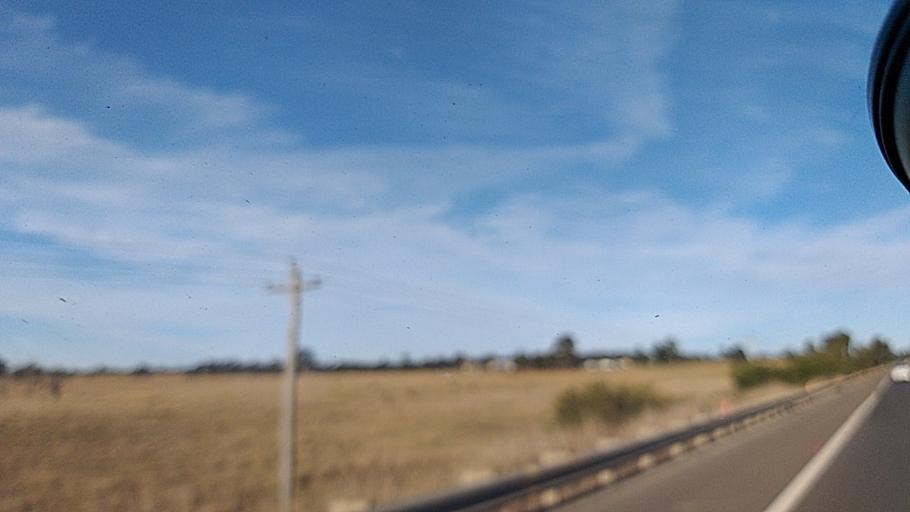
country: AU
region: New South Wales
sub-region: Blacktown
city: Riverstone
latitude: -33.6803
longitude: 150.8155
